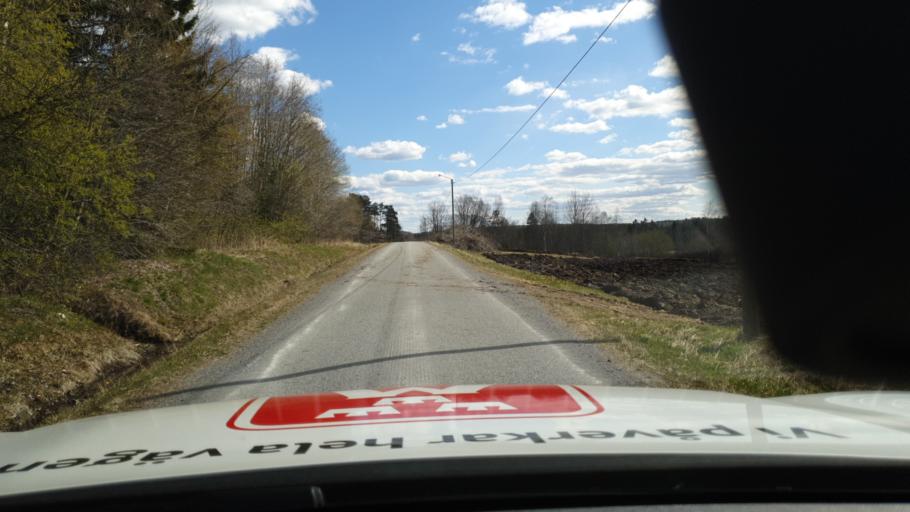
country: SE
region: Jaemtland
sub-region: Bergs Kommun
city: Hoverberg
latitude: 62.8334
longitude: 14.4143
